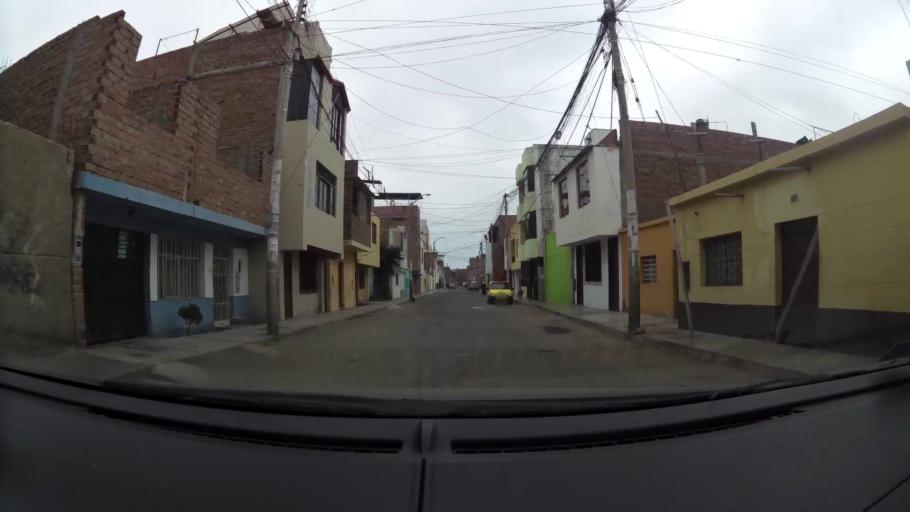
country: PE
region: La Libertad
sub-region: Provincia de Trujillo
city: Trujillo
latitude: -8.1047
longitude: -79.0394
